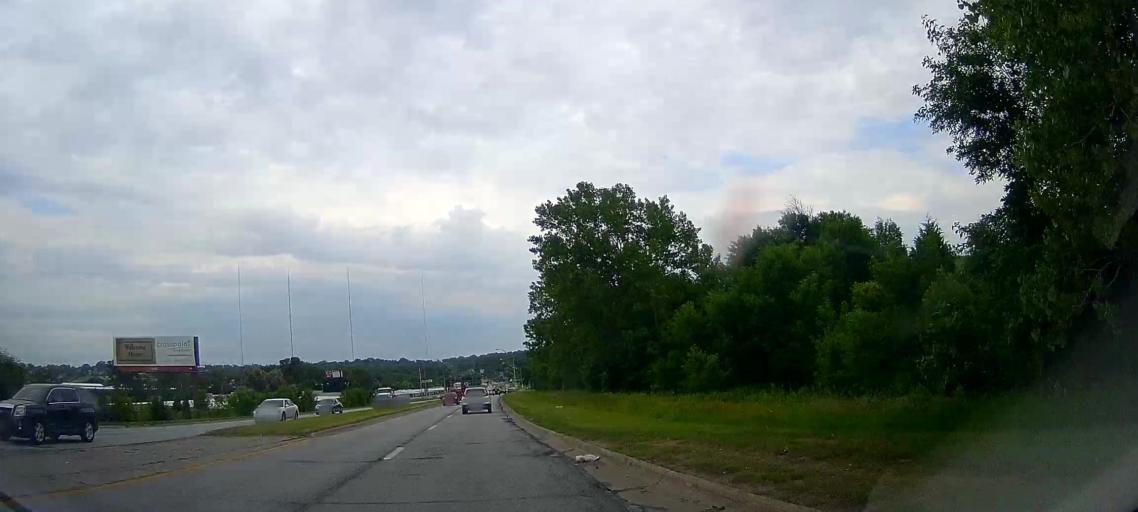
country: US
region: Nebraska
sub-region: Douglas County
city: Ralston
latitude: 41.3147
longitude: -96.0560
